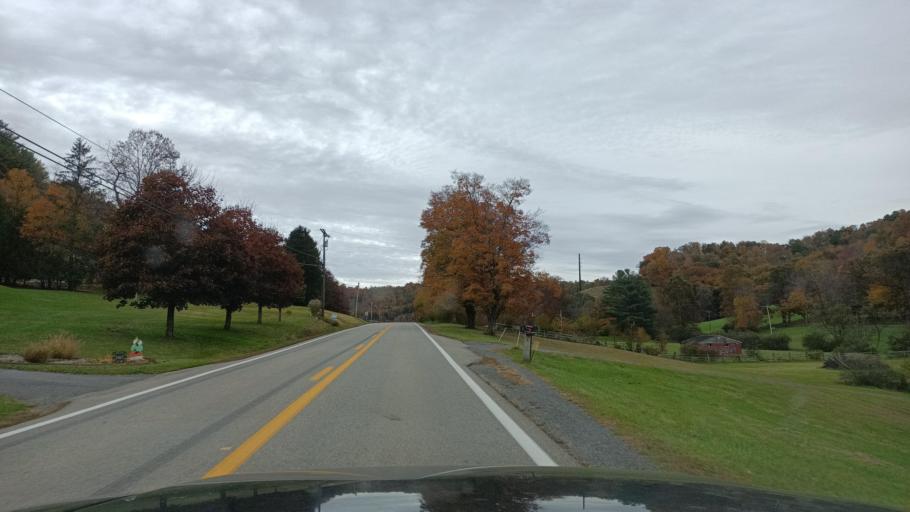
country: US
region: West Virginia
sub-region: Taylor County
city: Grafton
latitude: 39.3608
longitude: -79.9849
